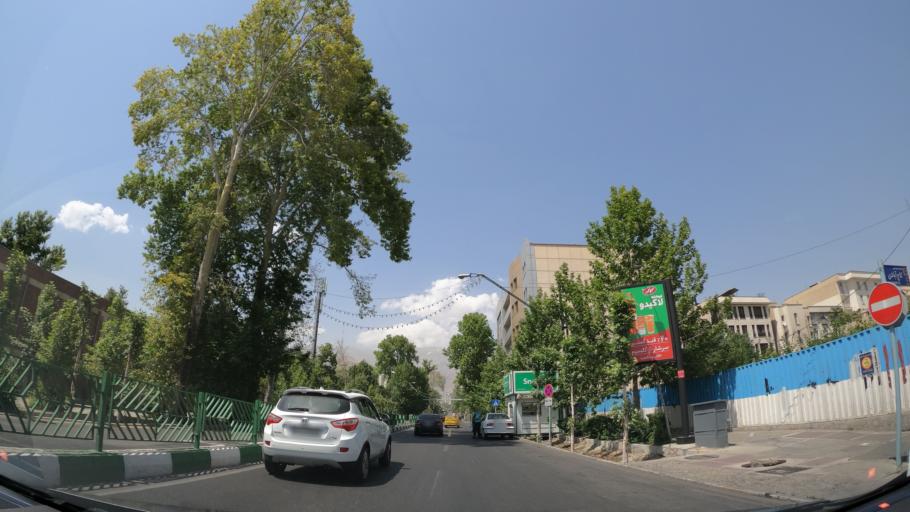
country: IR
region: Tehran
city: Tajrish
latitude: 35.7796
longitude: 51.4138
